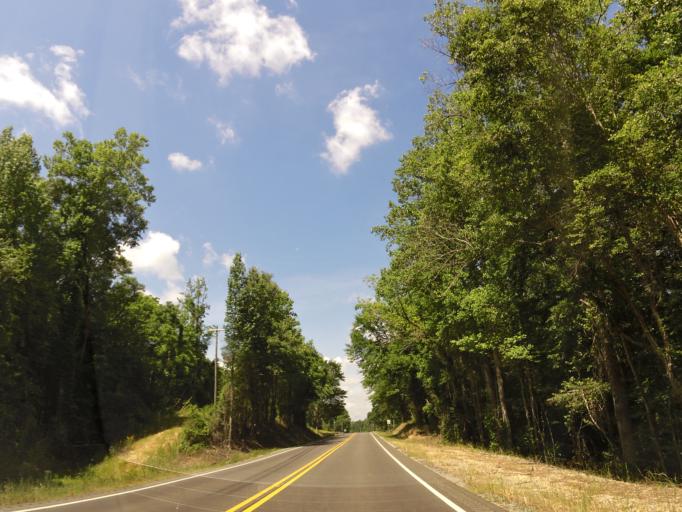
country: US
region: Alabama
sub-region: Marion County
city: Guin
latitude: 33.9355
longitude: -88.0082
